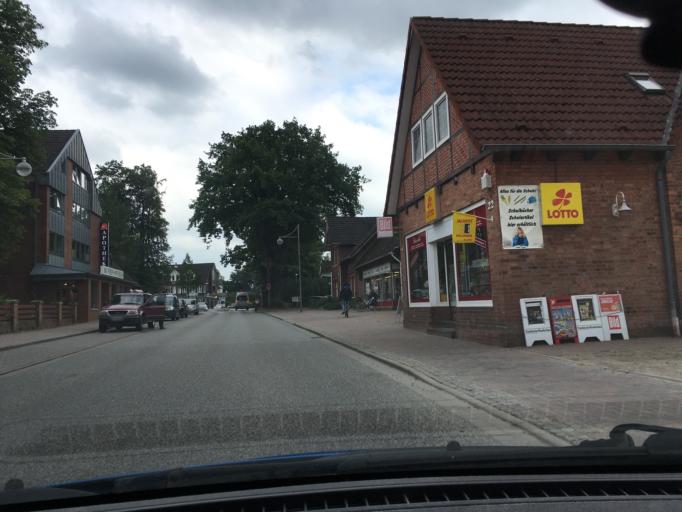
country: DE
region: Lower Saxony
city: Tostedt
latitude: 53.2788
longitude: 9.7152
